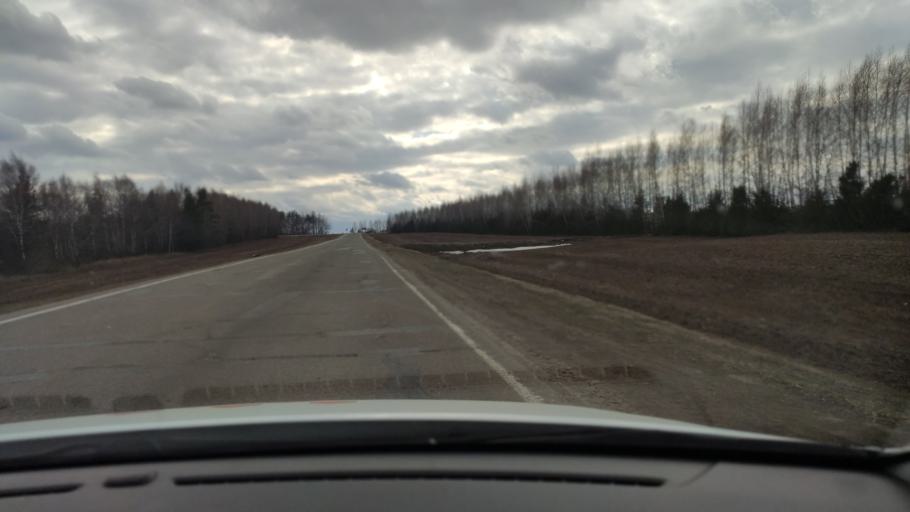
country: RU
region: Tatarstan
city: Vysokaya Gora
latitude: 56.1083
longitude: 49.1789
